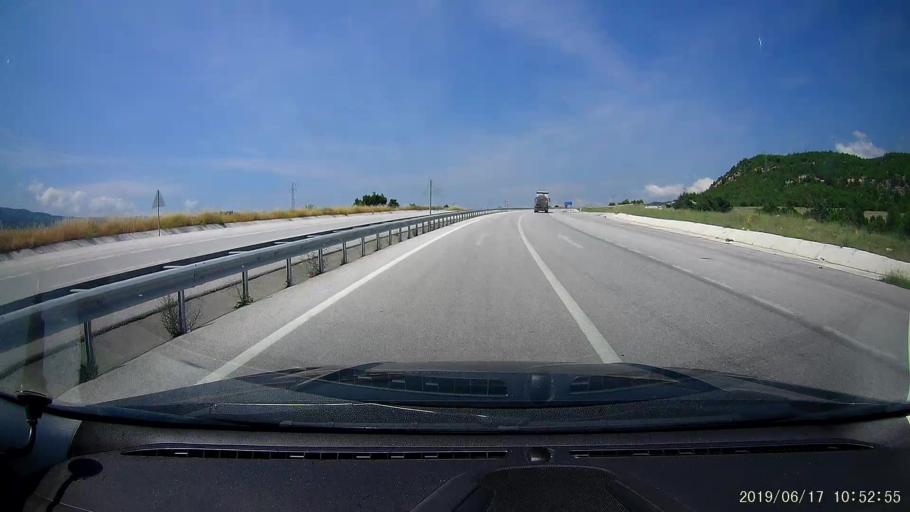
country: TR
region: Corum
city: Hacihamza
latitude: 41.0830
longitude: 34.3340
